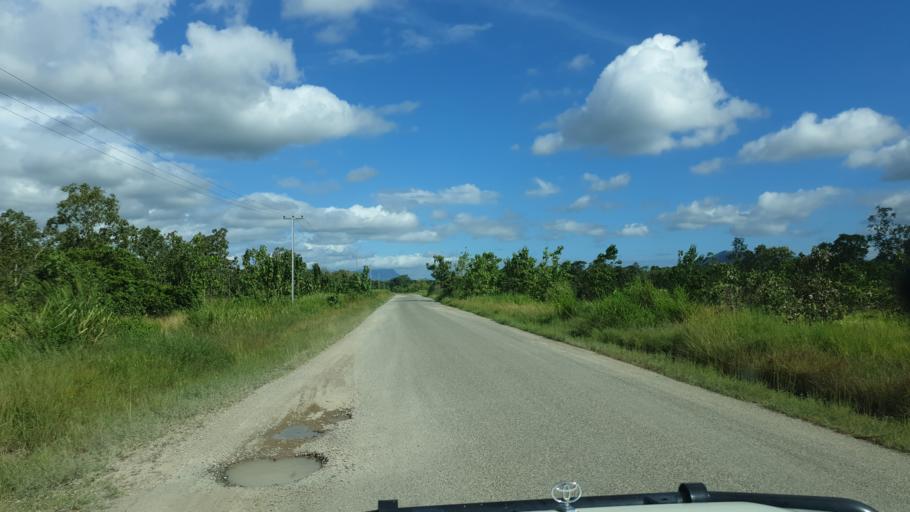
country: PG
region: National Capital
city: Port Moresby
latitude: -9.2609
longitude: 147.2299
